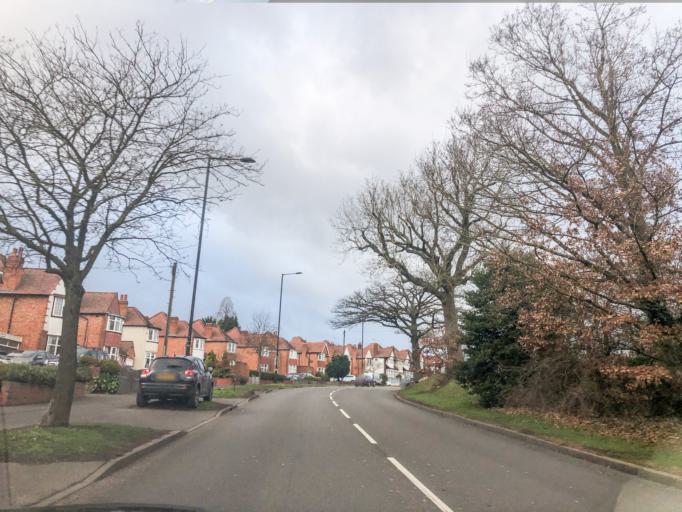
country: GB
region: England
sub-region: Solihull
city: Tidbury Green
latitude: 52.4161
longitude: -1.8893
